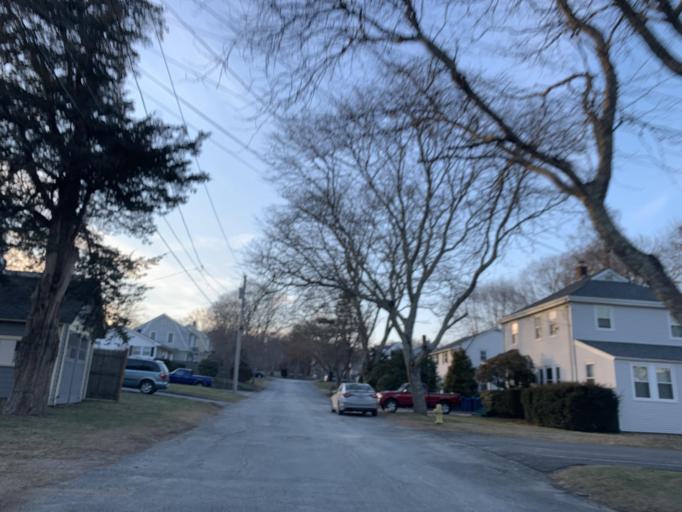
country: US
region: Rhode Island
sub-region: Washington County
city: Wakefield-Peacedale
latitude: 41.4468
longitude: -71.5039
